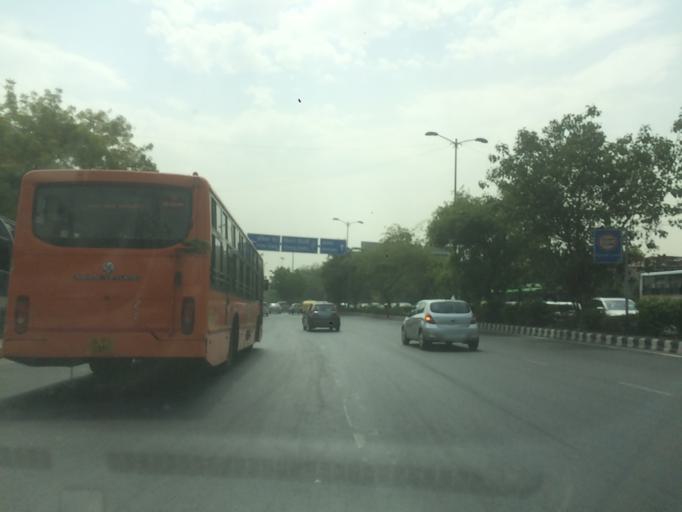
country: IN
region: NCT
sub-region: New Delhi
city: New Delhi
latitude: 28.5660
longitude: 77.2301
